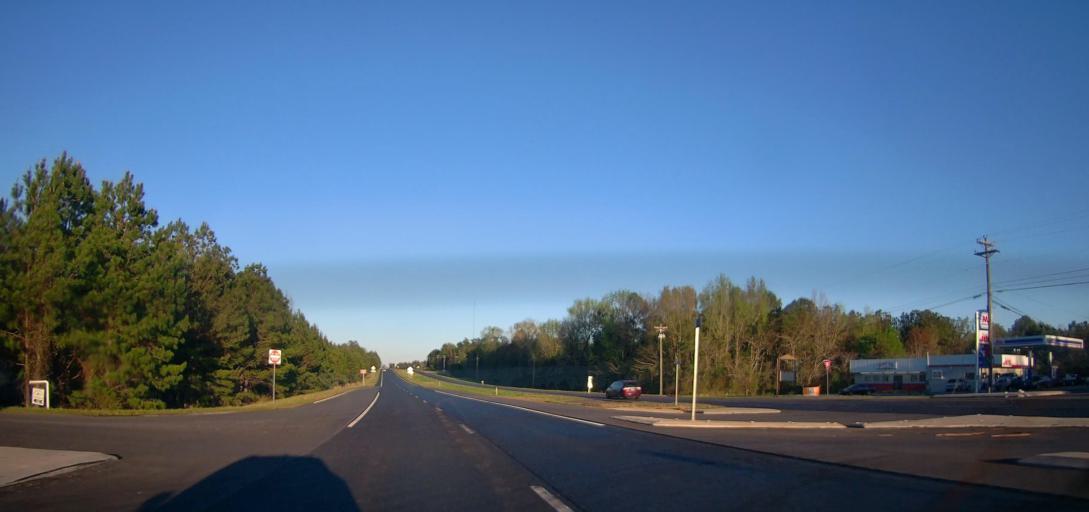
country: US
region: Georgia
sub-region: Bibb County
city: Macon
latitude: 32.8509
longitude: -83.4849
